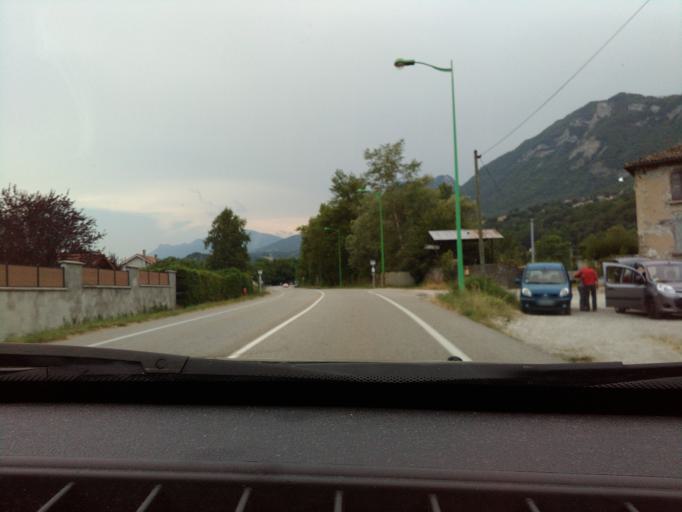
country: FR
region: Rhone-Alpes
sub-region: Departement de l'Isere
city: Vif
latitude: 45.0304
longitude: 5.6532
